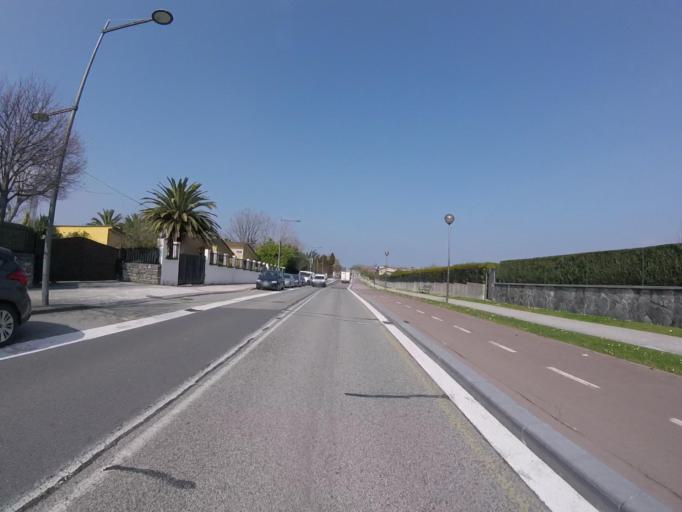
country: ES
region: Basque Country
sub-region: Provincia de Guipuzcoa
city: San Sebastian
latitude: 43.2899
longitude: -1.9902
